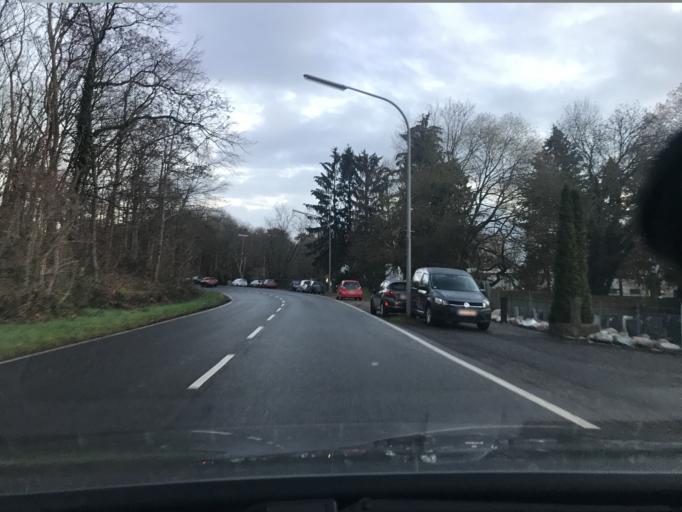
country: DE
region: North Rhine-Westphalia
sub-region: Regierungsbezirk Koln
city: Merheim
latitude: 50.9661
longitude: 7.0691
